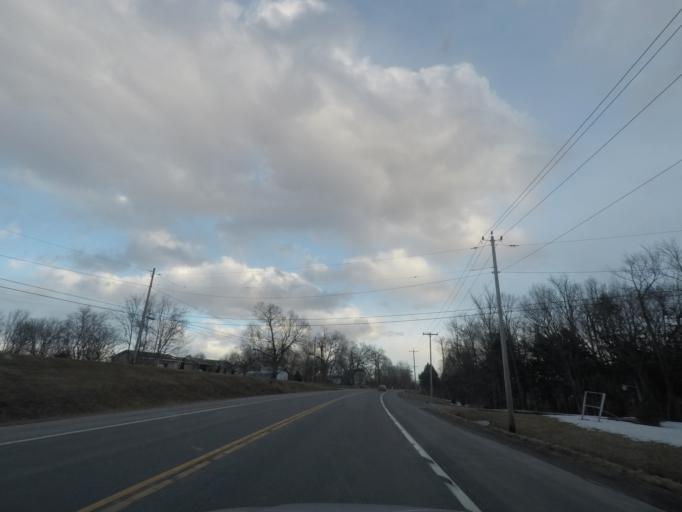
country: US
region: New York
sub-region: Herkimer County
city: Frankfort
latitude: 43.0812
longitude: -75.1181
